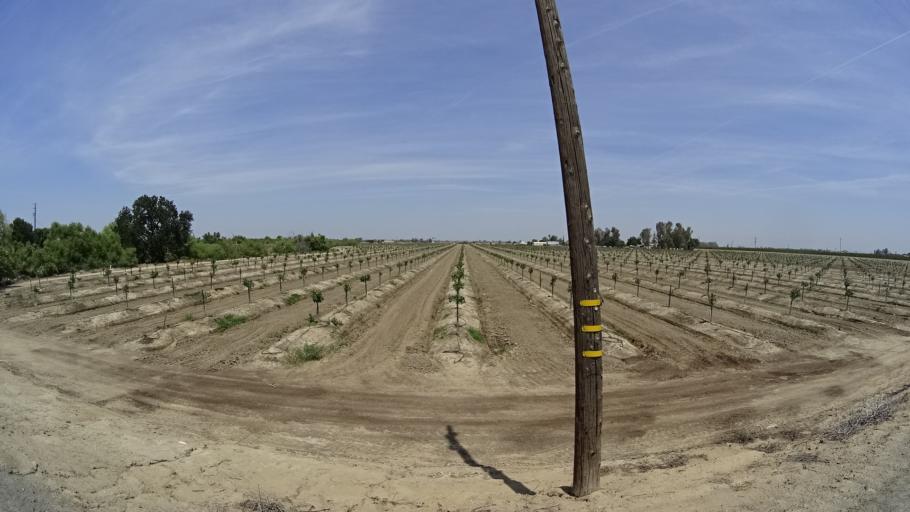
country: US
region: California
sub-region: Fresno County
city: Riverdale
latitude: 36.3874
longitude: -119.8538
